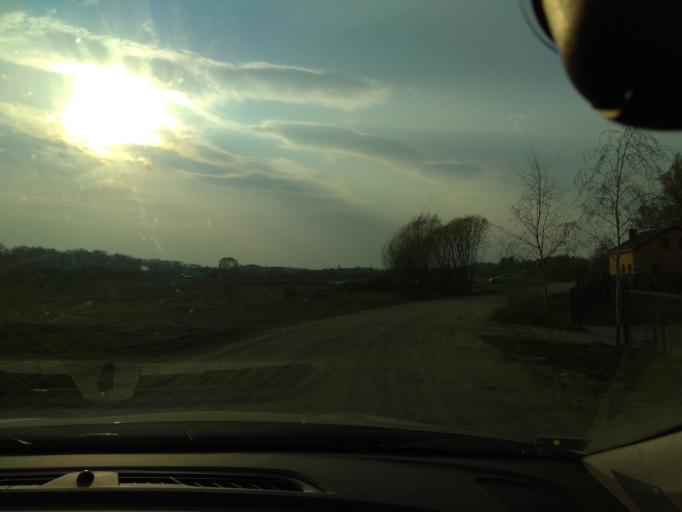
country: LT
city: Baltoji Voke
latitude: 54.5952
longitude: 25.1813
